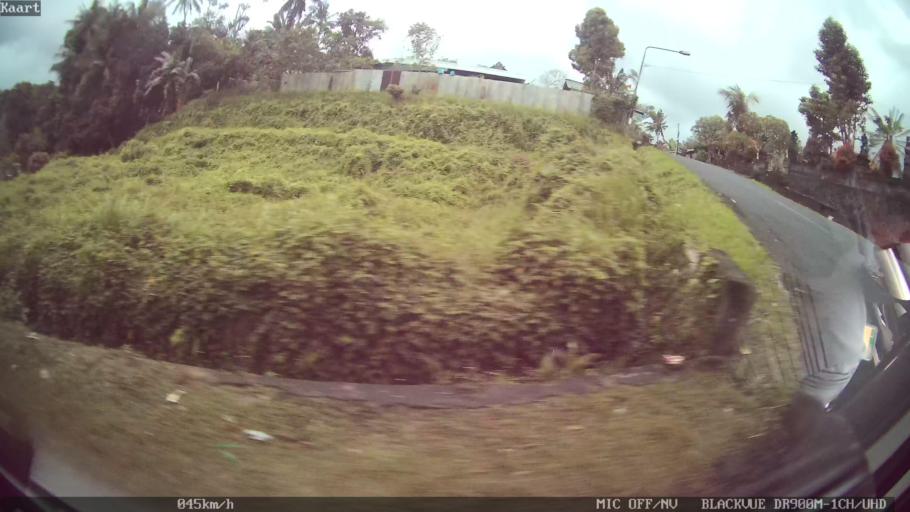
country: ID
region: Bali
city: Banjar Sayanbaleran
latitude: -8.5248
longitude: 115.1845
